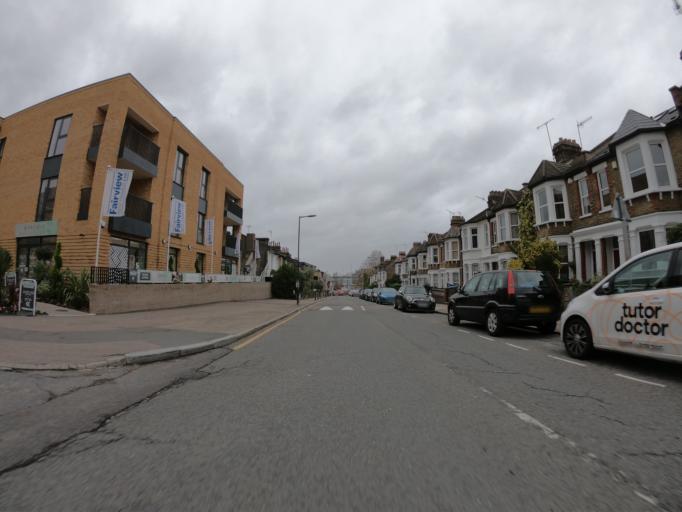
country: GB
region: England
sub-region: Greater London
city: Blackheath
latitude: 51.4861
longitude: 0.0253
